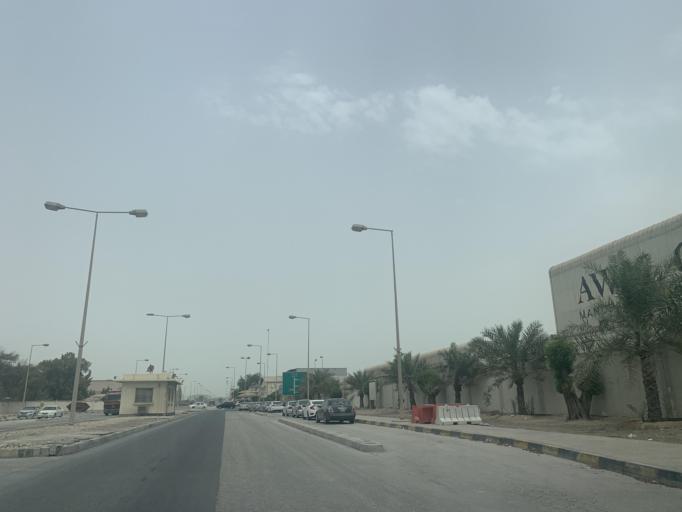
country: BH
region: Northern
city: Sitrah
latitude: 26.1775
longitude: 50.6155
